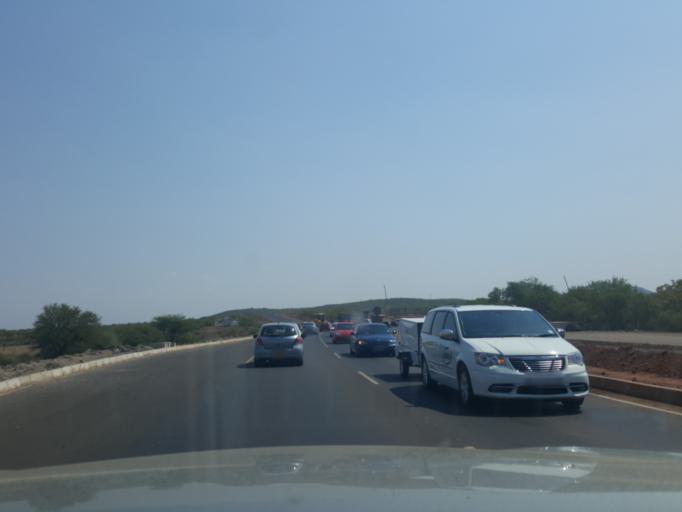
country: BW
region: South East
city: Ramotswa
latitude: -24.8229
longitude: 25.8097
